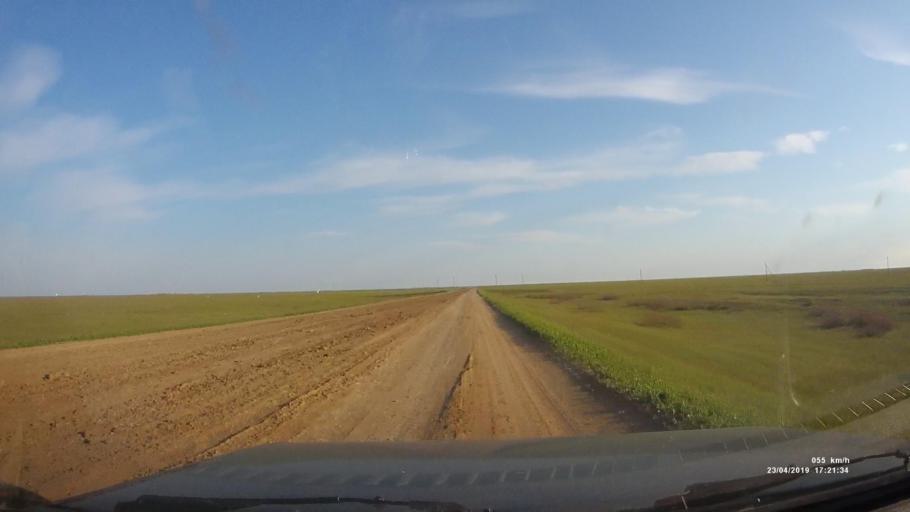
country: RU
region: Kalmykiya
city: Priyutnoye
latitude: 46.1751
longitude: 43.5055
